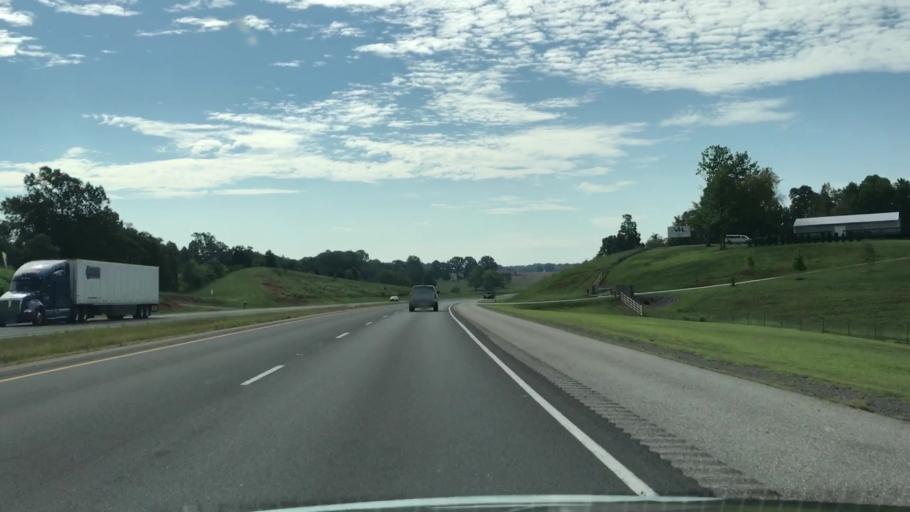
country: US
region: Kentucky
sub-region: Warren County
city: Plano
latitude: 36.8338
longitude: -86.3157
